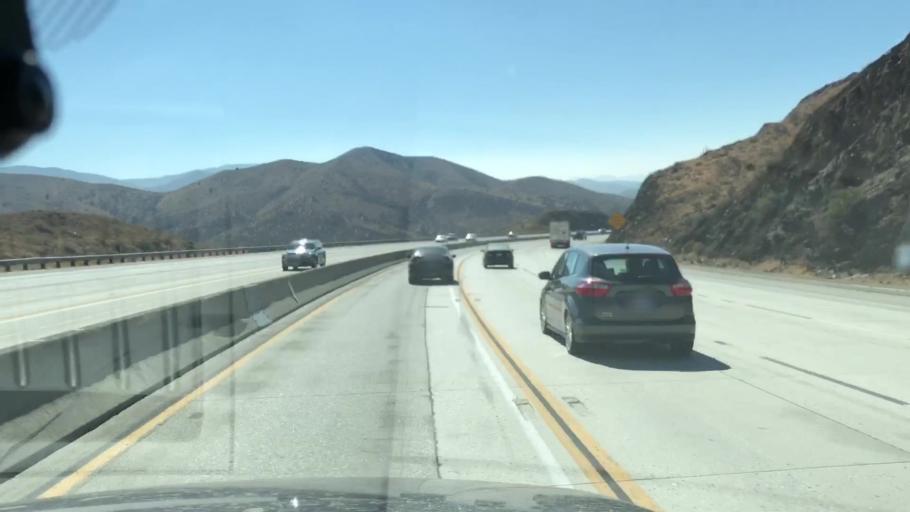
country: US
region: California
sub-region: Los Angeles County
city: Agua Dulce
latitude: 34.4834
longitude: -118.2877
